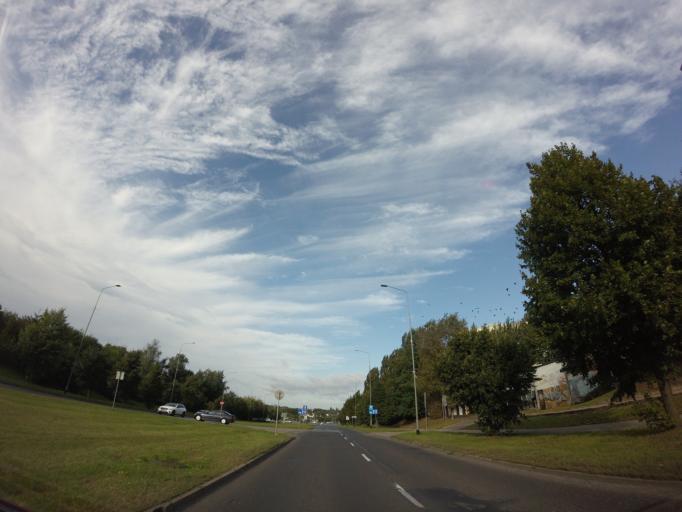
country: PL
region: West Pomeranian Voivodeship
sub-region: Szczecin
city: Szczecin
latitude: 53.4288
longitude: 14.5039
